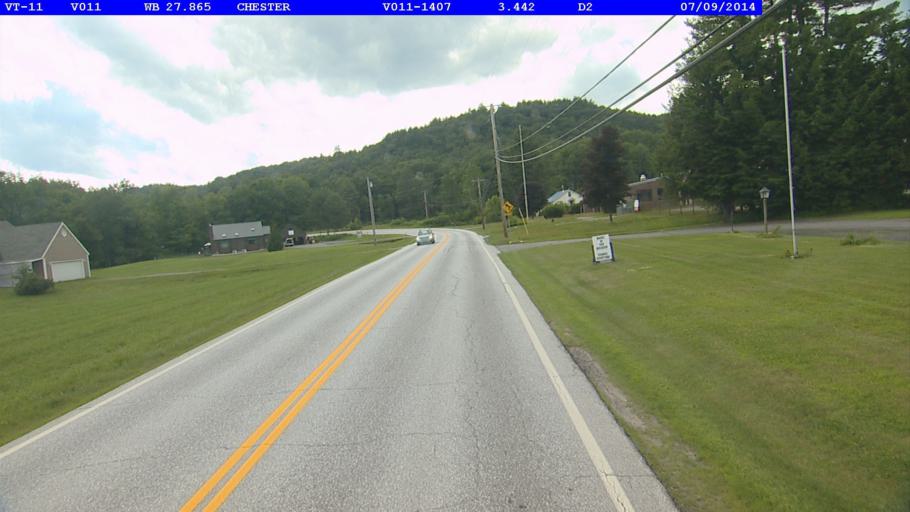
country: US
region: Vermont
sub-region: Windsor County
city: Chester
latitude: 43.2702
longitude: -72.6258
